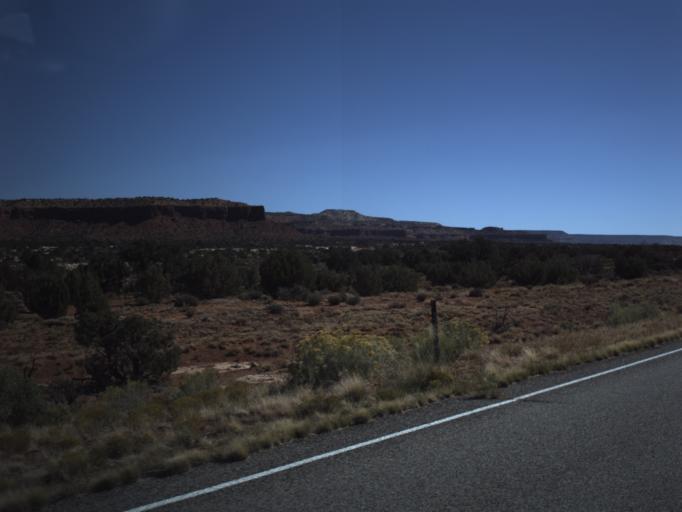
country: US
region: Utah
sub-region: San Juan County
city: Blanding
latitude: 37.6766
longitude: -110.2117
